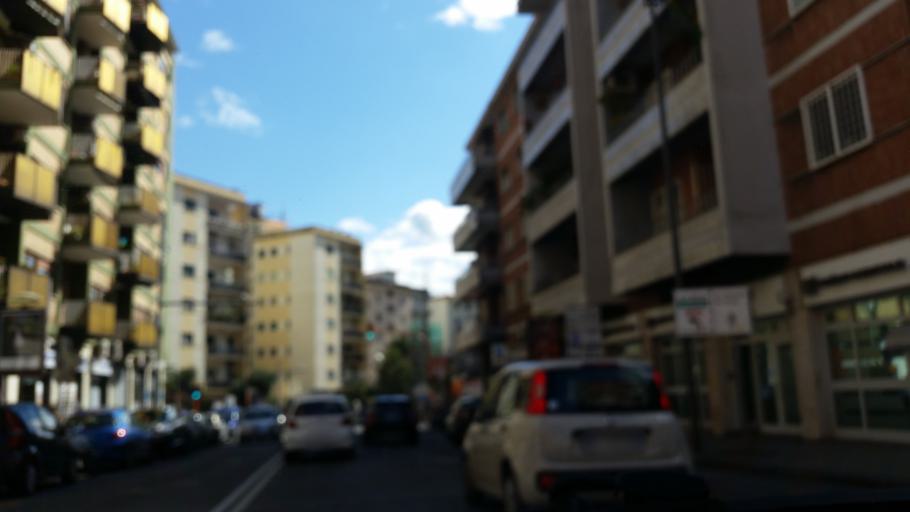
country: IT
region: Campania
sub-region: Provincia di Napoli
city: Napoli
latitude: 40.8407
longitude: 14.2175
